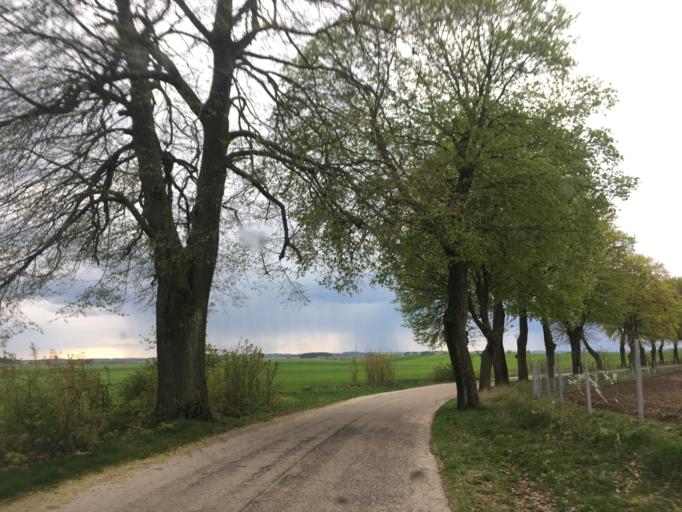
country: PL
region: Warmian-Masurian Voivodeship
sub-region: Powiat ostrodzki
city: Dabrowno
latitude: 53.4132
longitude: 20.1387
